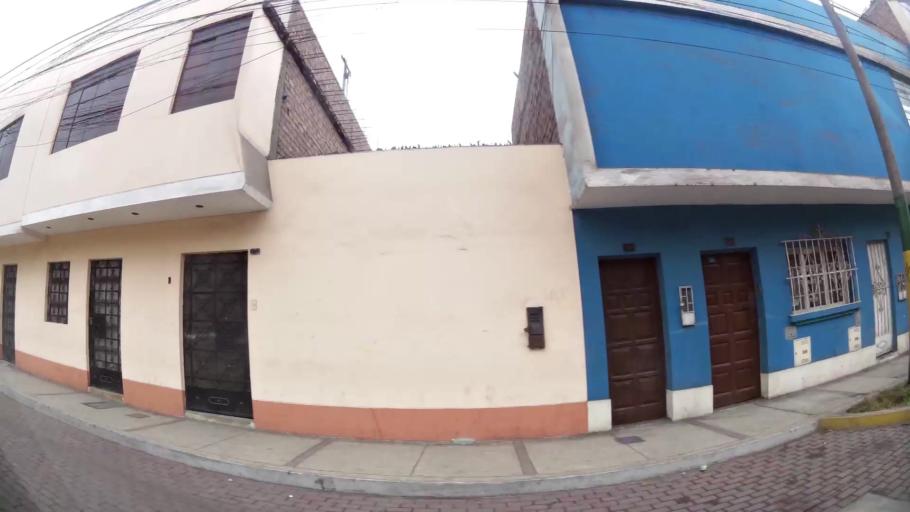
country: PE
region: Lima
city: Lima
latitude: -12.0488
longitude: -77.0048
